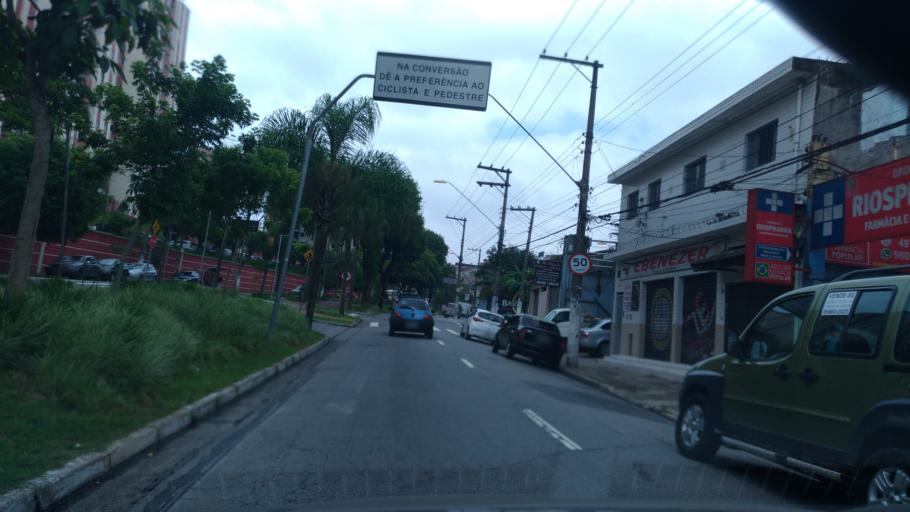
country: BR
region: Sao Paulo
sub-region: Santo Andre
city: Santo Andre
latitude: -23.6946
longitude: -46.5117
